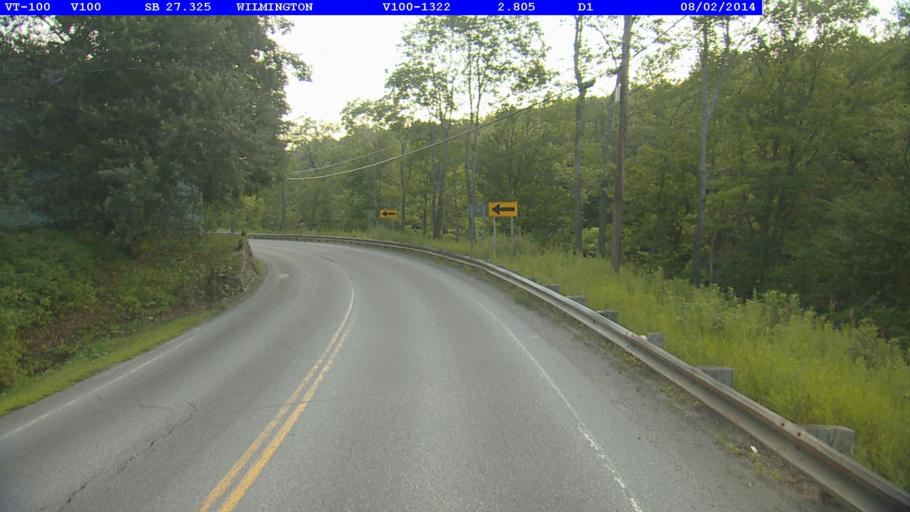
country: US
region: Vermont
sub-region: Windham County
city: Dover
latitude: 42.8716
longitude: -72.8663
